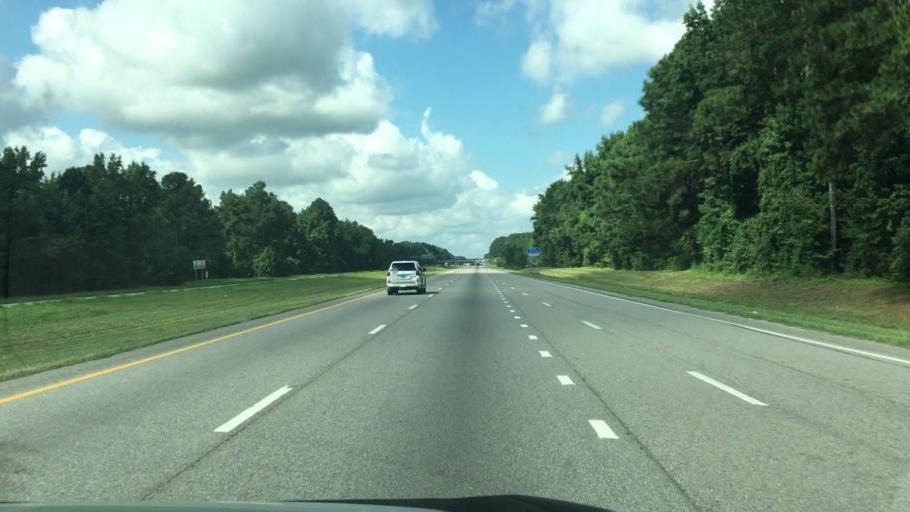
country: US
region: North Carolina
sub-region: Robeson County
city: Fairmont
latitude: 34.5744
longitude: -79.1560
